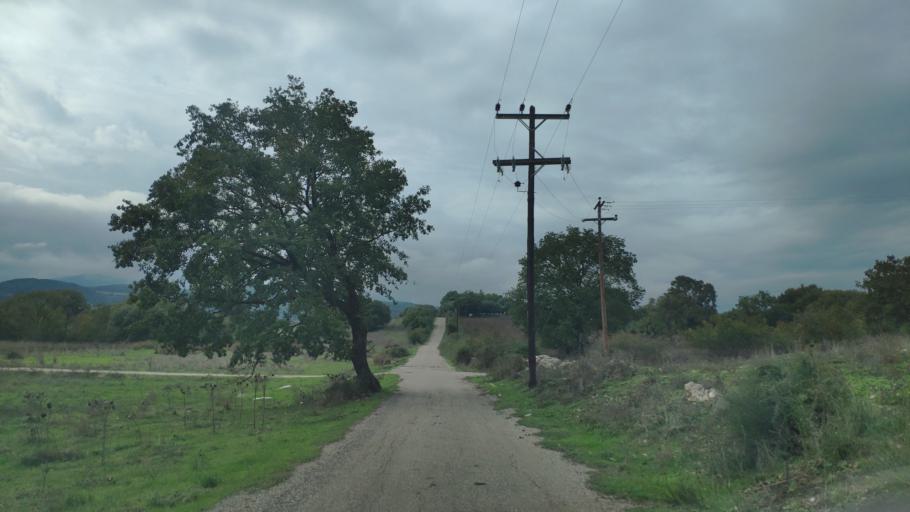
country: GR
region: West Greece
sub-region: Nomos Aitolias kai Akarnanias
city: Monastirakion
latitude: 38.9204
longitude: 21.0069
